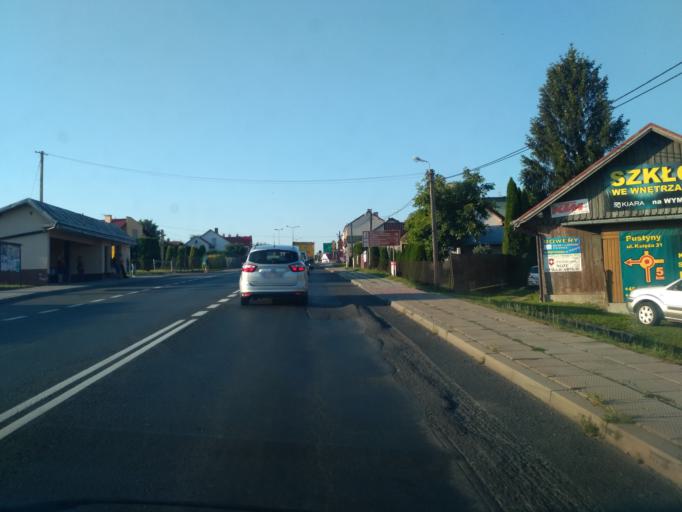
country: PL
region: Subcarpathian Voivodeship
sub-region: Powiat krosnienski
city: Miejsce Piastowe
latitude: 49.6365
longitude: 21.7863
